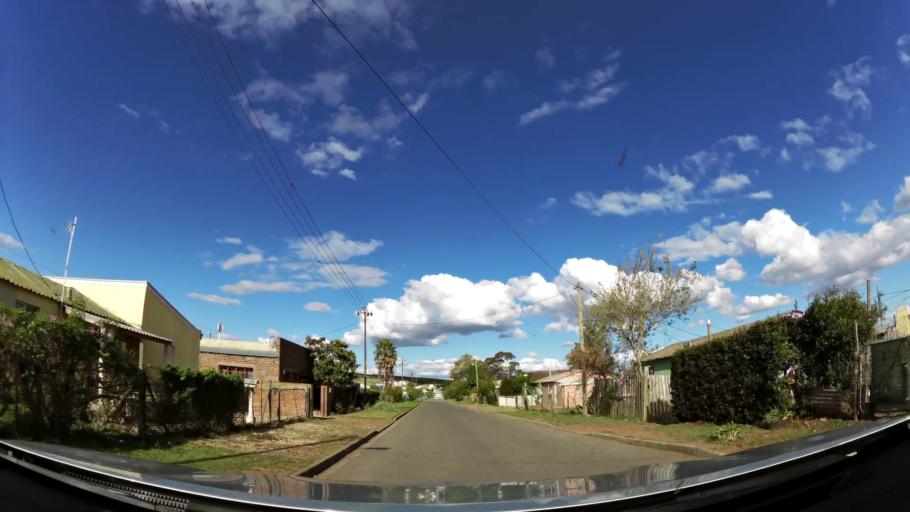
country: ZA
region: Western Cape
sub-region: Overberg District Municipality
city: Swellendam
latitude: -34.0354
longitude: 20.4420
